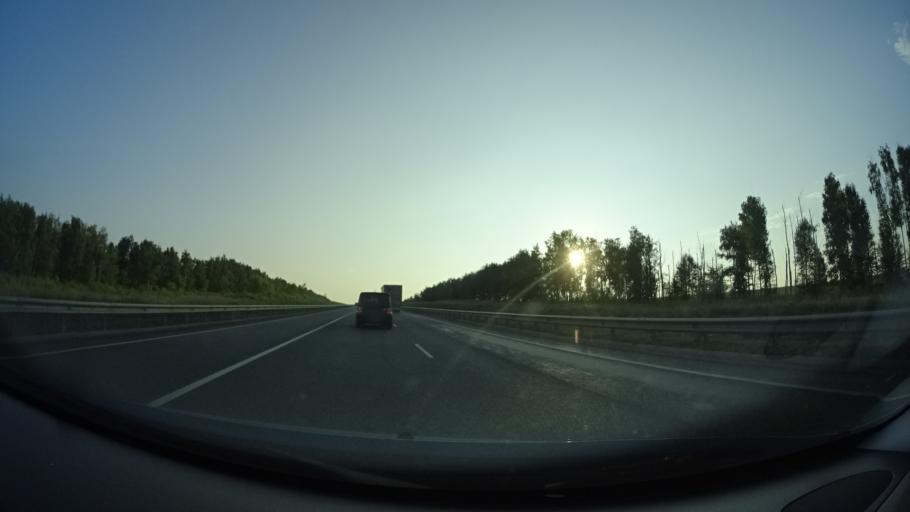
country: RU
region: Samara
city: Klyavlino
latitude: 54.0250
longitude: 51.8717
